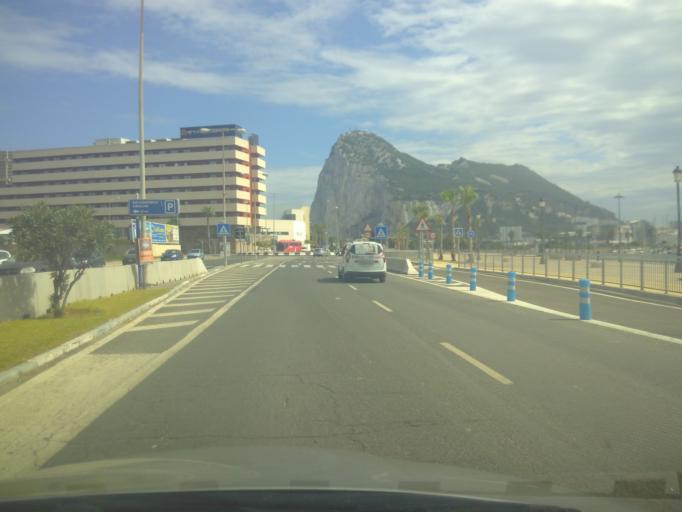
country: ES
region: Andalusia
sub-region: Provincia de Cadiz
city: La Linea de la Concepcion
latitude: 36.1595
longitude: -5.3543
